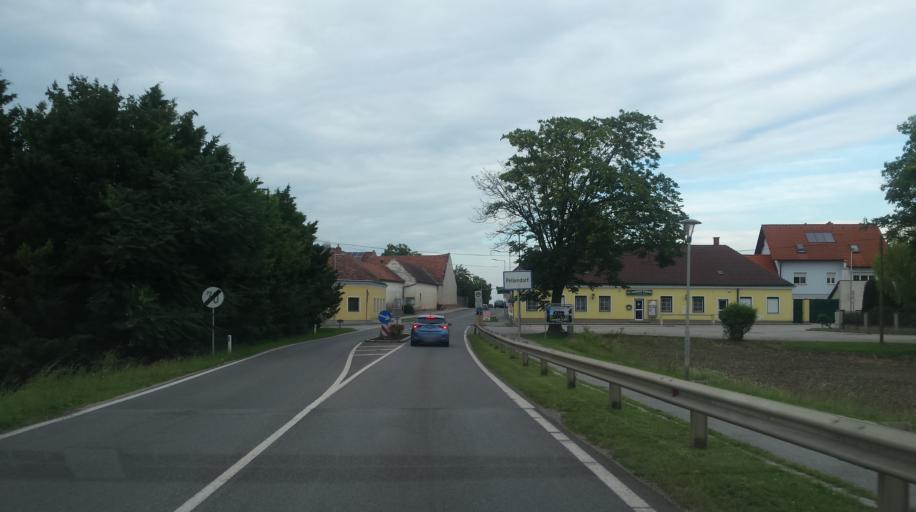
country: AT
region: Lower Austria
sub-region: Politischer Bezirk Wien-Umgebung
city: Zwolfaxing
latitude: 48.0968
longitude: 16.4539
